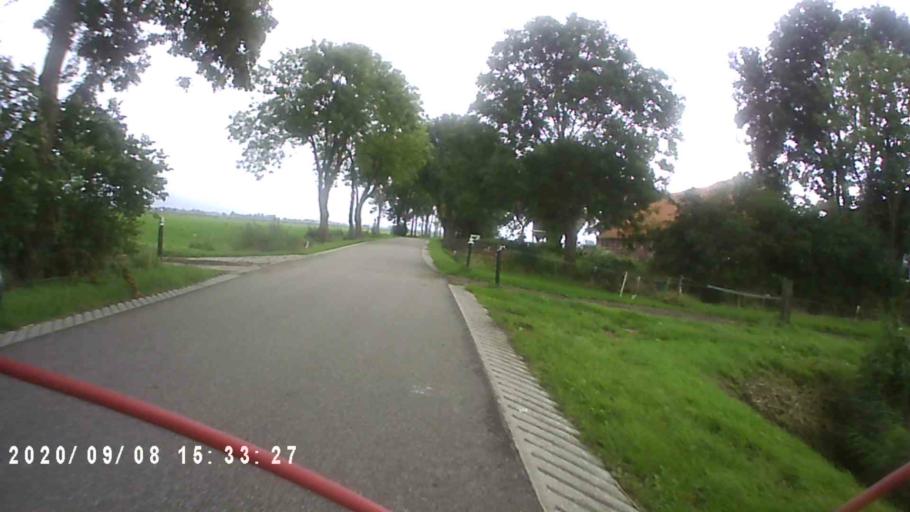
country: NL
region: Groningen
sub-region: Gemeente Bedum
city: Bedum
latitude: 53.2927
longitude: 6.6316
